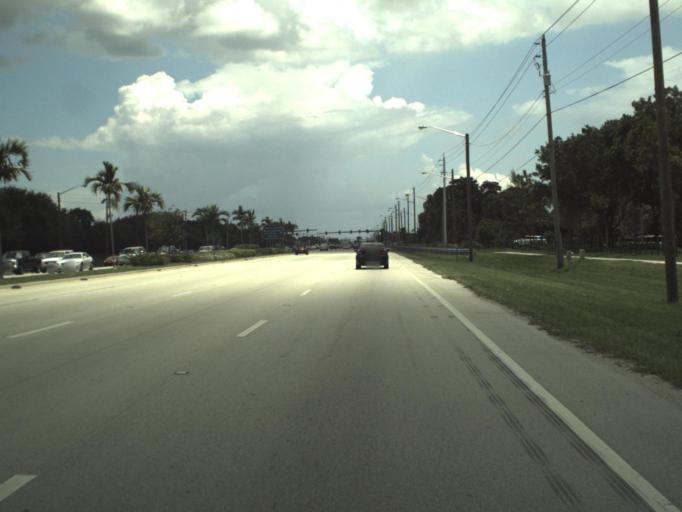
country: US
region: Florida
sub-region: Palm Beach County
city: Plantation Mobile Home Park
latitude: 26.7081
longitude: -80.1615
